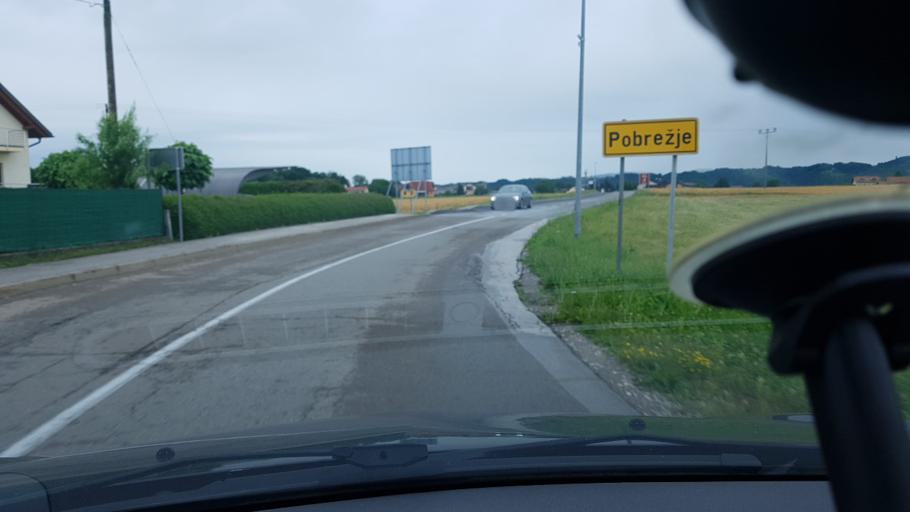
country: SI
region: Hajdina
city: Spodnja Hajdina
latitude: 46.3895
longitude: 15.8701
